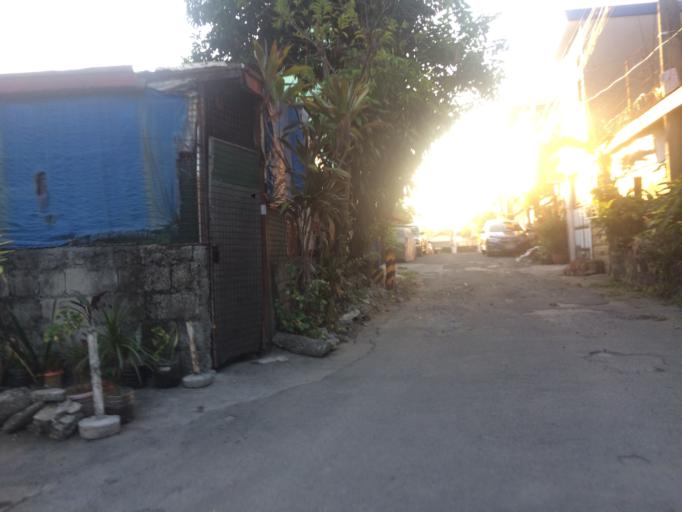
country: PH
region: Calabarzon
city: Bagong Pagasa
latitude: 14.6749
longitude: 121.0178
